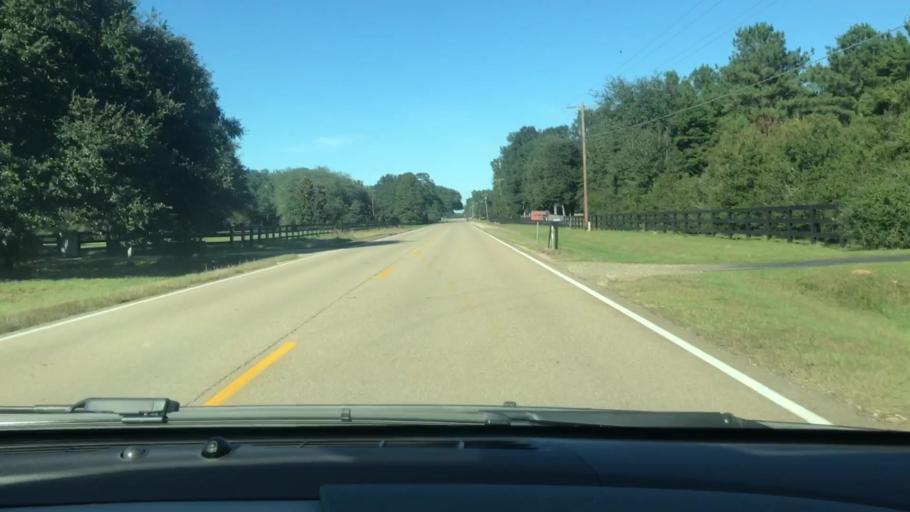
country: US
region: Louisiana
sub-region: Saint Tammany Parish
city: Abita Springs
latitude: 30.5906
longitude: -90.0323
